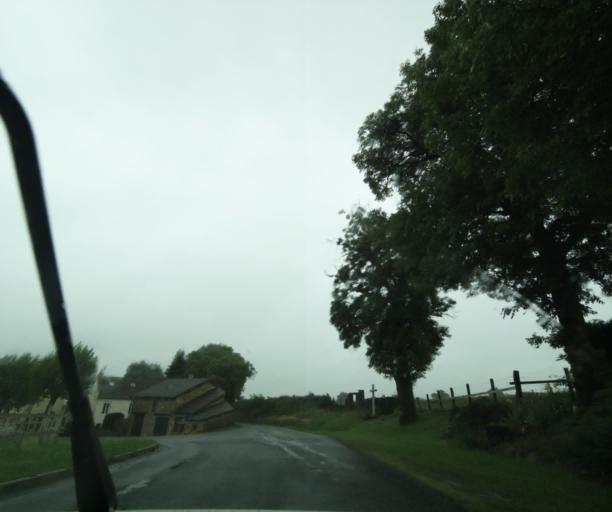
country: FR
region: Bourgogne
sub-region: Departement de Saone-et-Loire
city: Charolles
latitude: 46.4261
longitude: 4.2800
